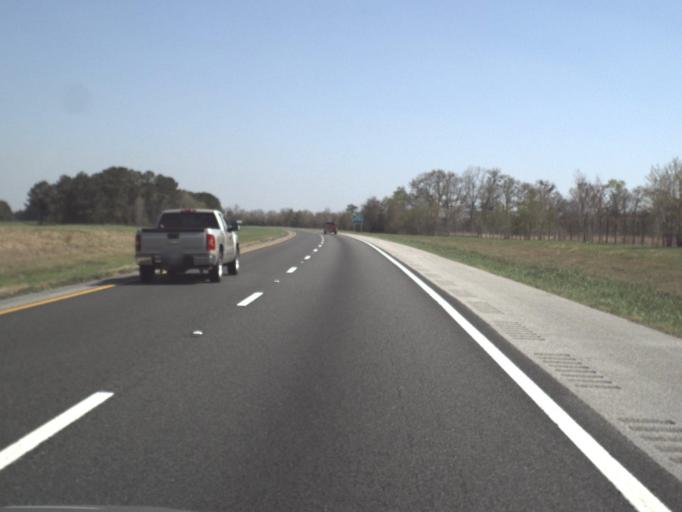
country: US
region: Florida
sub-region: Jackson County
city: Sneads
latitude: 30.6422
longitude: -85.0034
